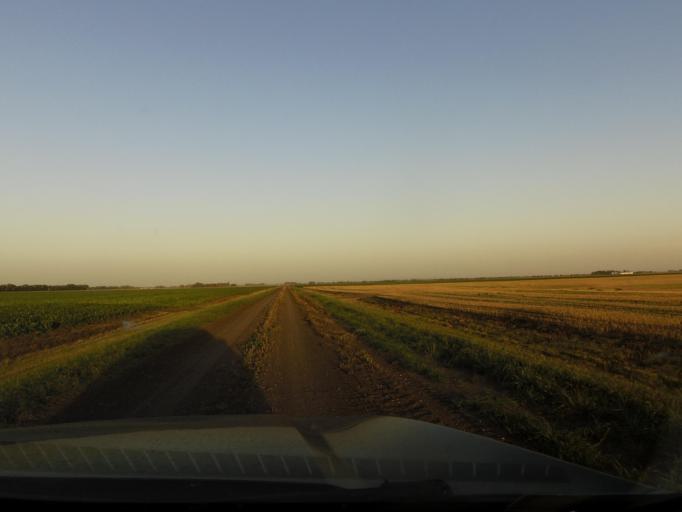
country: US
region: North Dakota
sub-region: Walsh County
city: Grafton
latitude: 48.3829
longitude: -97.2502
